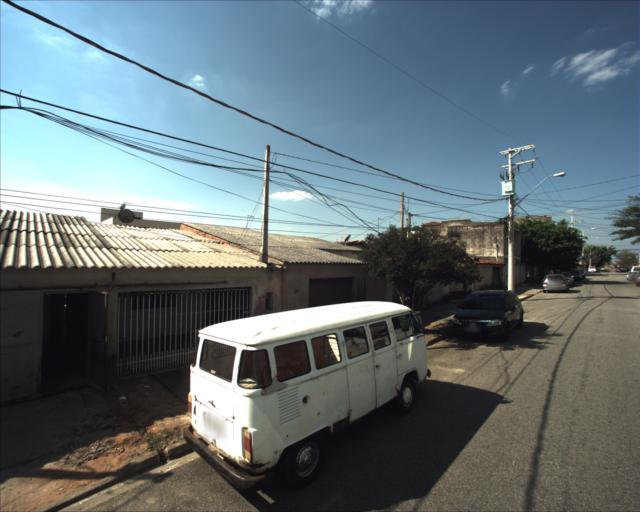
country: BR
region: Sao Paulo
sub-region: Sorocaba
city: Sorocaba
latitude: -23.5006
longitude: -47.5178
